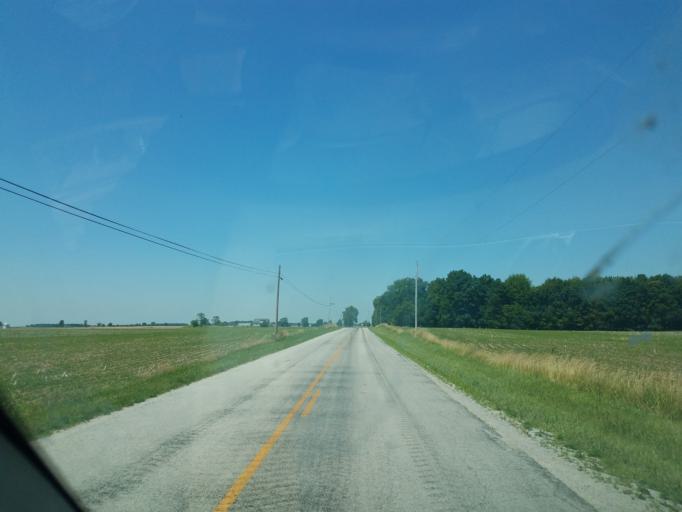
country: US
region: Ohio
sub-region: Hardin County
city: Kenton
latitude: 40.6800
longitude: -83.5381
